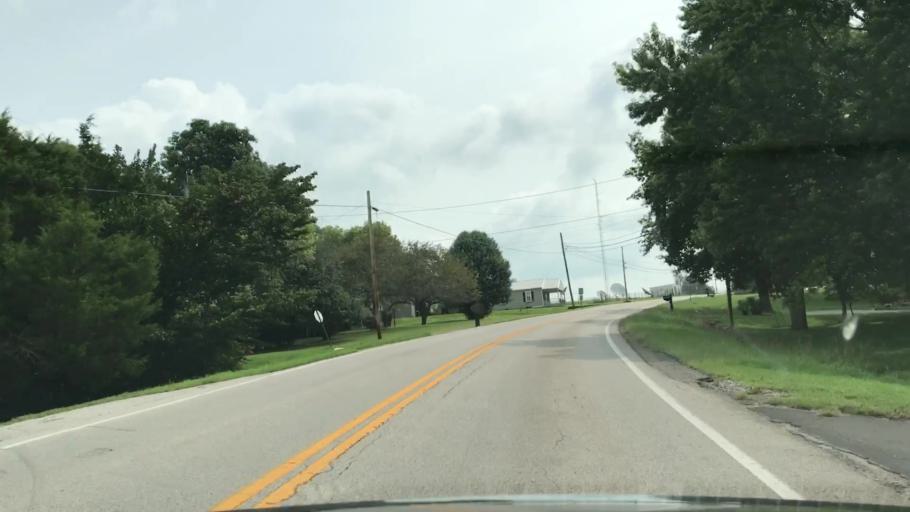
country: US
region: Kentucky
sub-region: Barren County
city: Cave City
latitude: 37.0960
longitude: -86.0384
